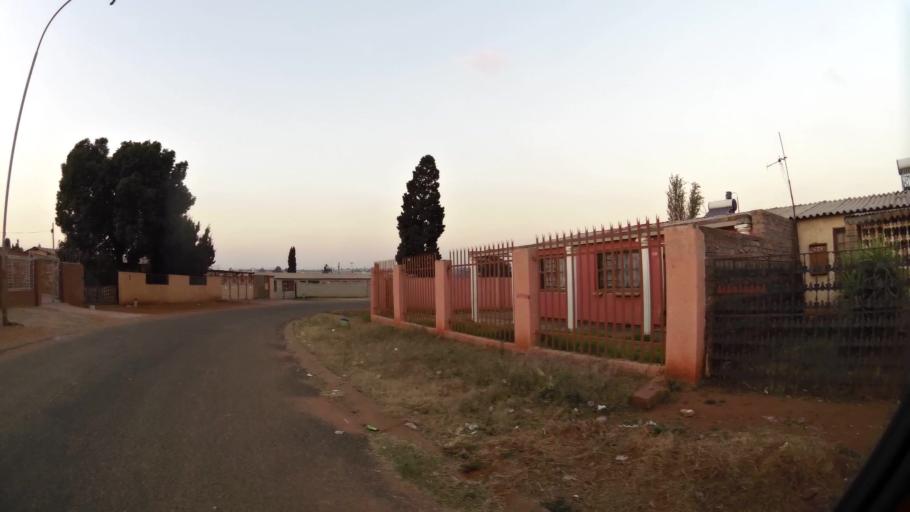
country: ZA
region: Gauteng
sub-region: City of Johannesburg Metropolitan Municipality
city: Soweto
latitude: -26.2880
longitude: 27.8799
